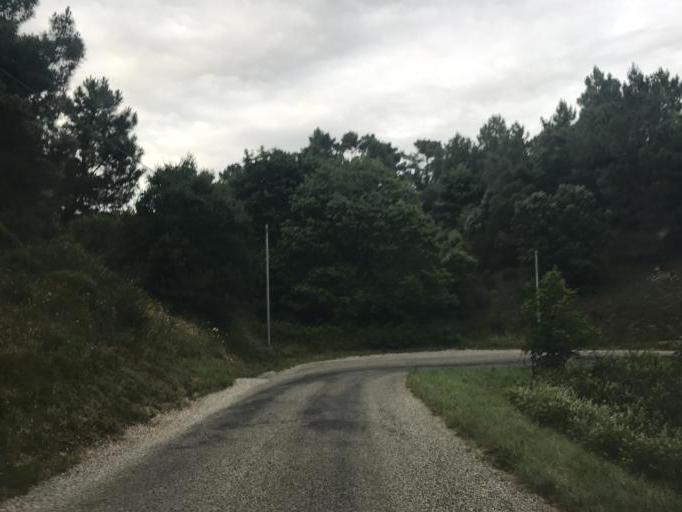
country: FR
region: Rhone-Alpes
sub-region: Departement de l'Ardeche
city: Saint-Laurent-du-Pape
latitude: 44.8051
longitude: 4.7484
